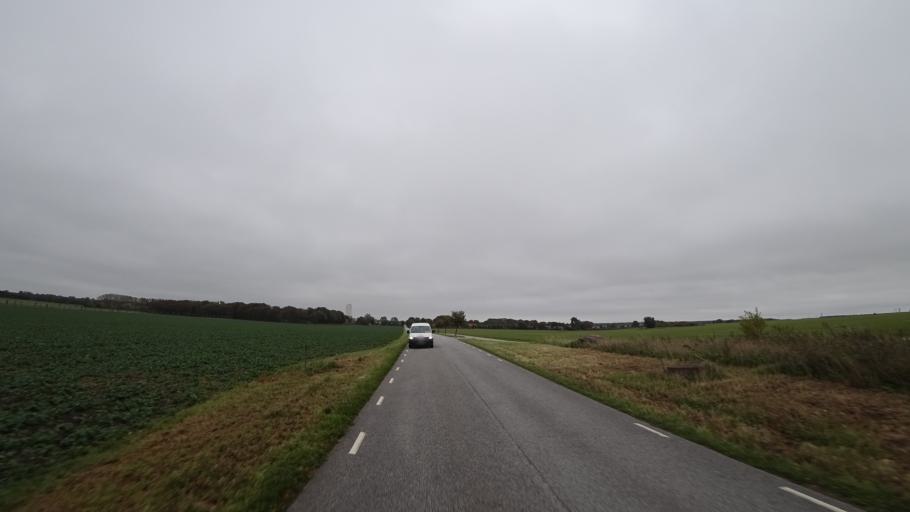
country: SE
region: Skane
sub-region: Kavlinge Kommun
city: Hofterup
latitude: 55.7721
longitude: 12.9401
